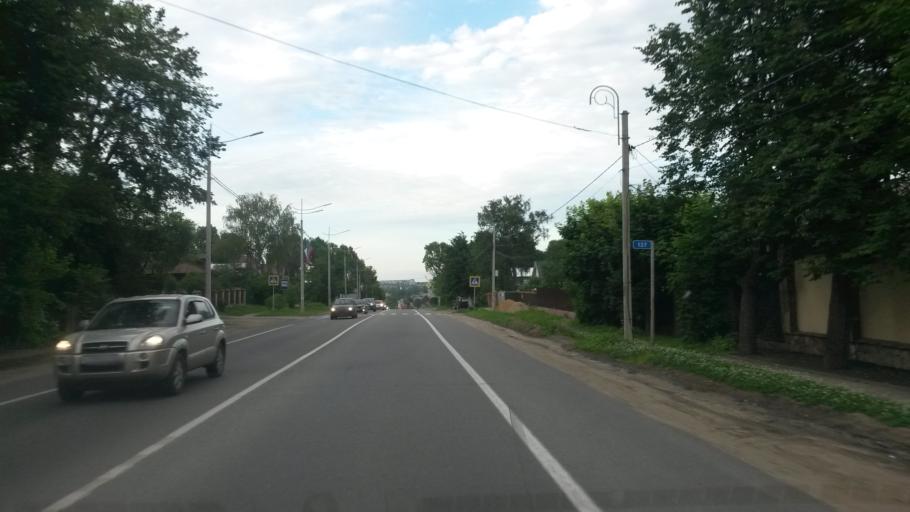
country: RU
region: Jaroslavl
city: Pereslavl'-Zalesskiy
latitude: 56.7180
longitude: 38.8254
